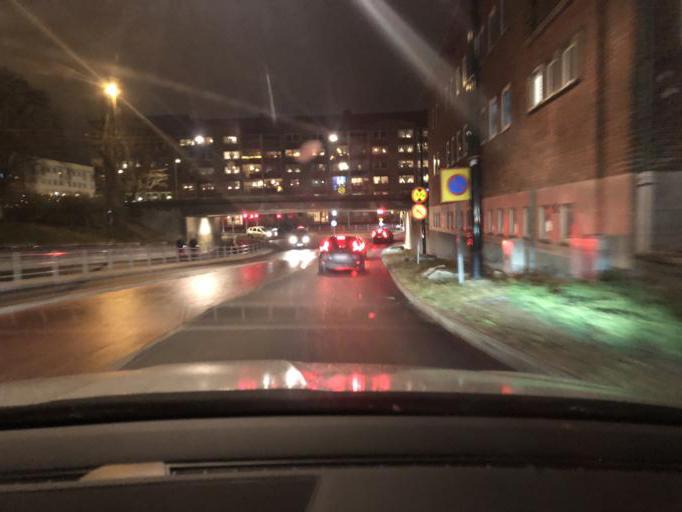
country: SE
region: Vaermland
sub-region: Karlstads Kommun
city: Karlstad
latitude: 59.3770
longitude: 13.5051
